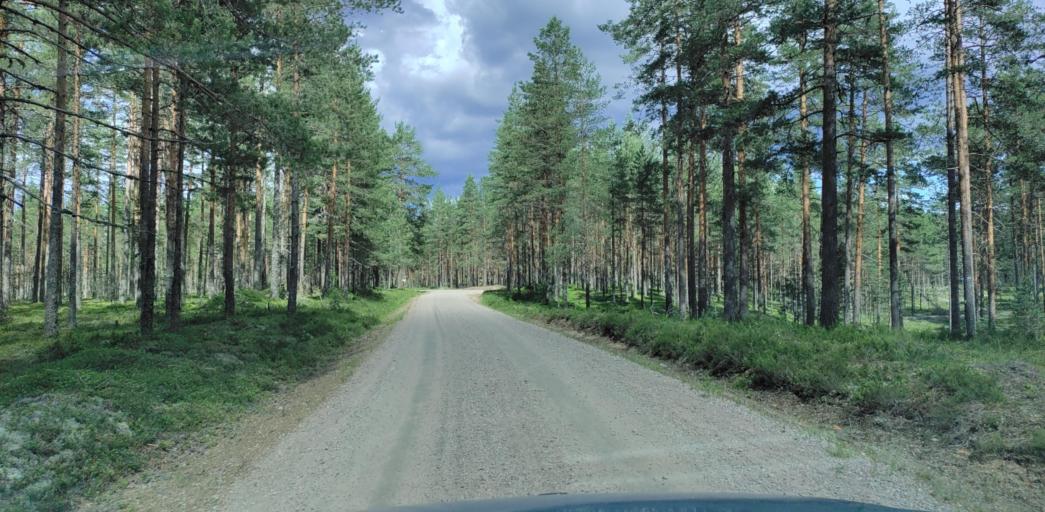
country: SE
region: Vaermland
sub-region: Hagfors Kommun
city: Ekshaerad
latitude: 60.0599
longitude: 13.2884
